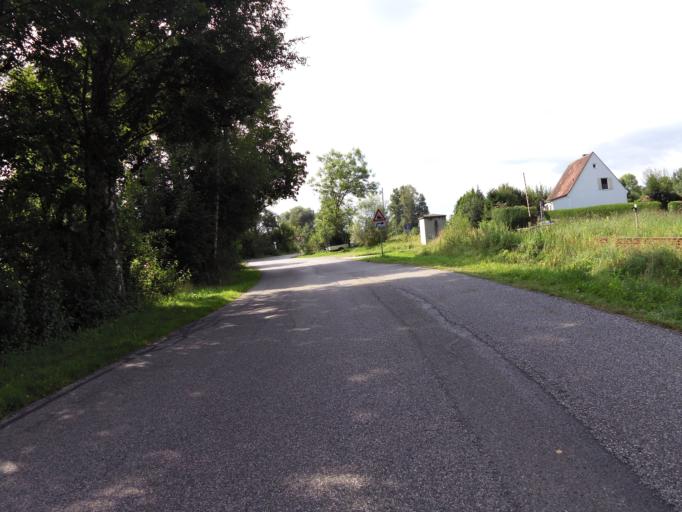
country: DE
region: Bavaria
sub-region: Upper Bavaria
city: Diessen am Ammersee
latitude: 47.9409
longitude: 11.1068
